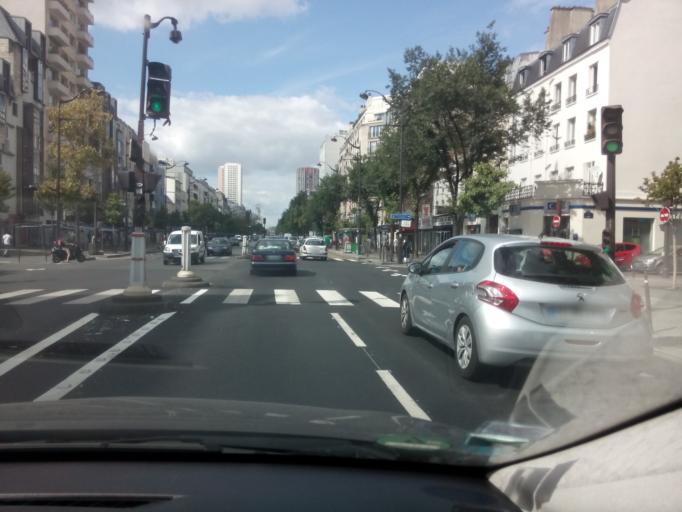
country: FR
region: Ile-de-France
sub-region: Departement du Val-de-Marne
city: Le Kremlin-Bicetre
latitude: 48.8220
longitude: 2.3587
